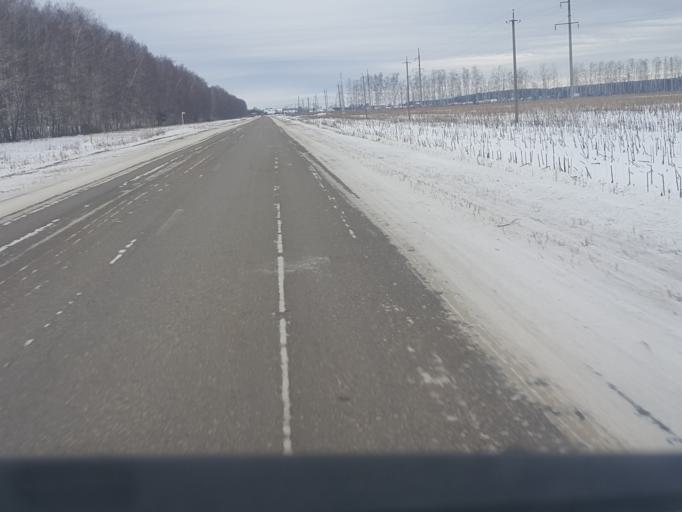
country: RU
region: Tambov
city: Rasskazovo
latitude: 52.8163
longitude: 41.7952
